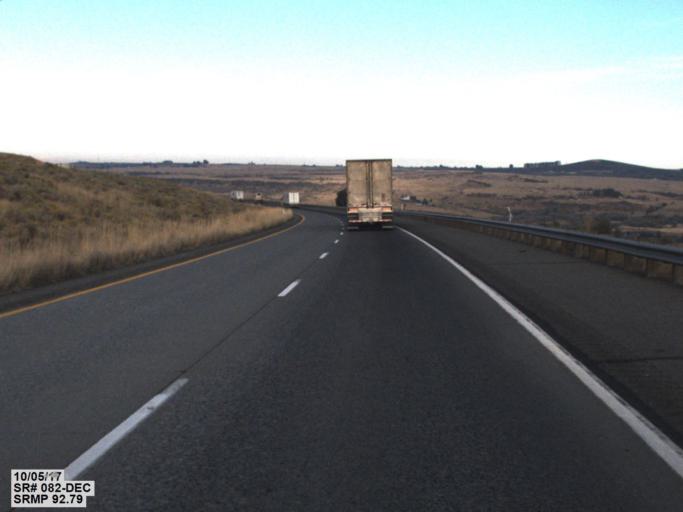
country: US
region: Washington
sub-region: Benton County
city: Benton City
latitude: 46.2676
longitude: -119.5513
